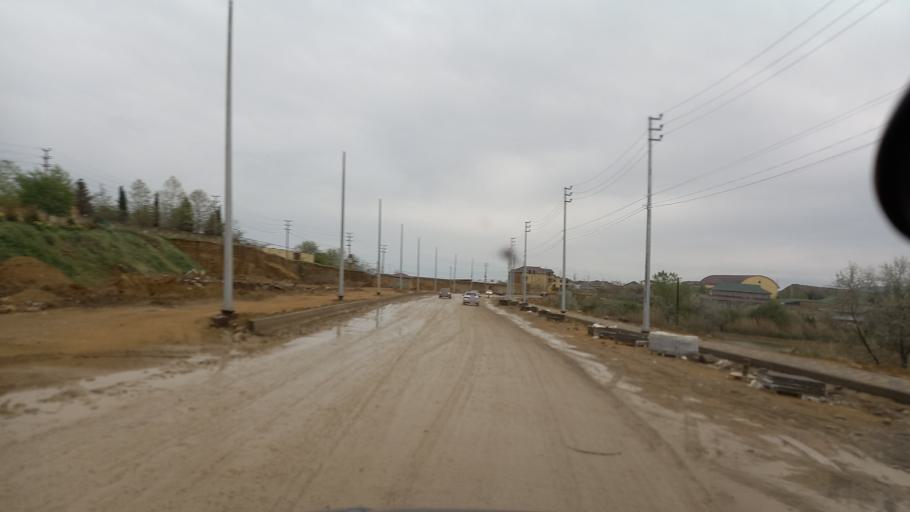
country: RU
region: Dagestan
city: Derbent
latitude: 42.0974
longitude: 48.2868
